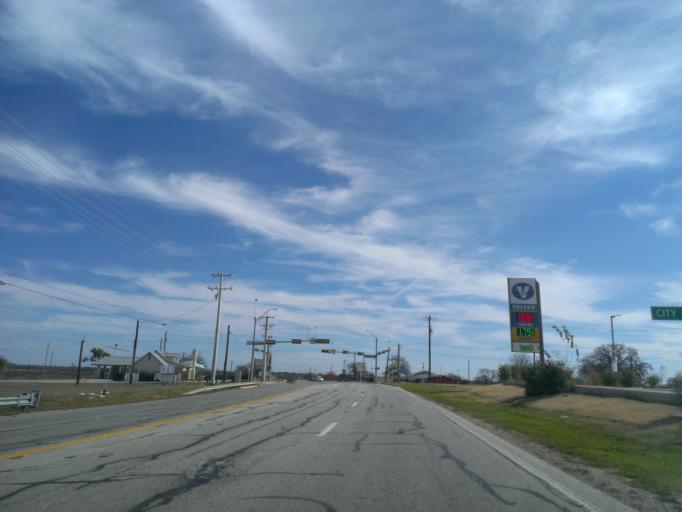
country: US
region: Texas
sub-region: Burnet County
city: Granite Shoals
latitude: 30.6056
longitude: -98.3722
